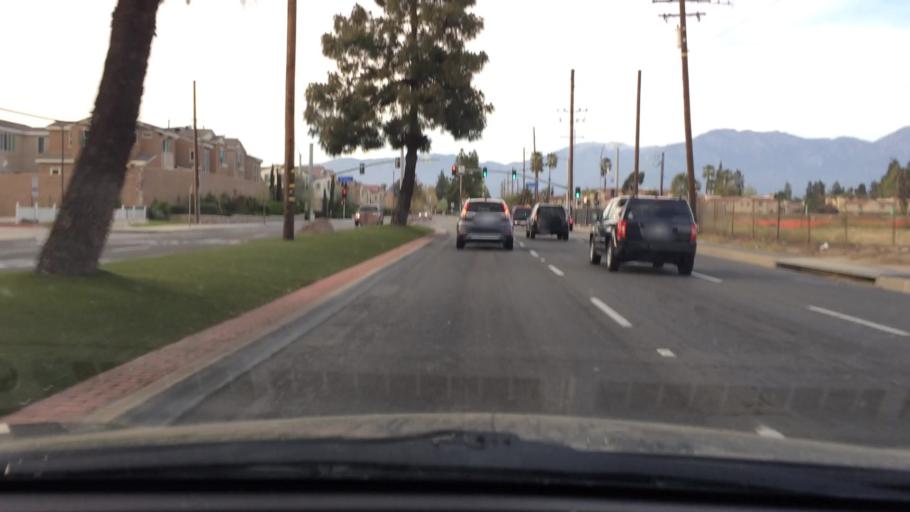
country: US
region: California
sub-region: San Bernardino County
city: Chino
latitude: 34.0421
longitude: -117.6895
